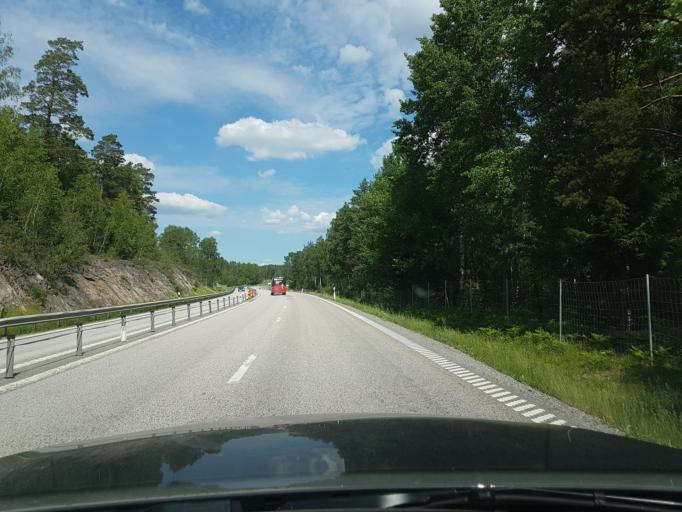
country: SE
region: Stockholm
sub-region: Vallentuna Kommun
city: Vallentuna
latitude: 59.5260
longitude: 18.1886
